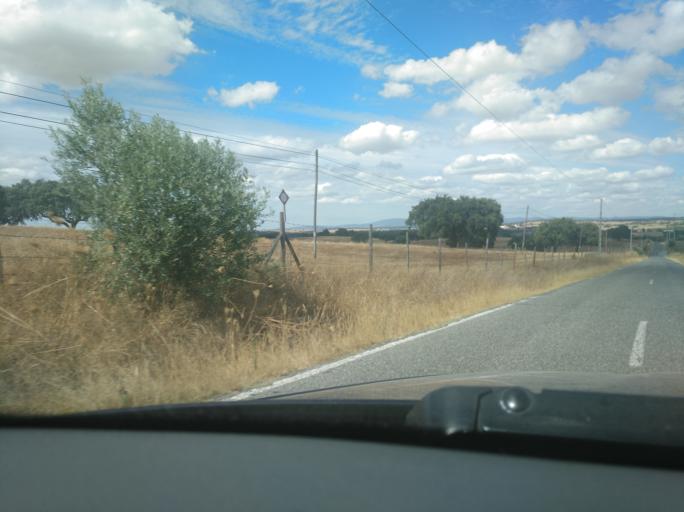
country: PT
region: Portalegre
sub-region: Arronches
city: Arronches
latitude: 39.0656
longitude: -7.4034
